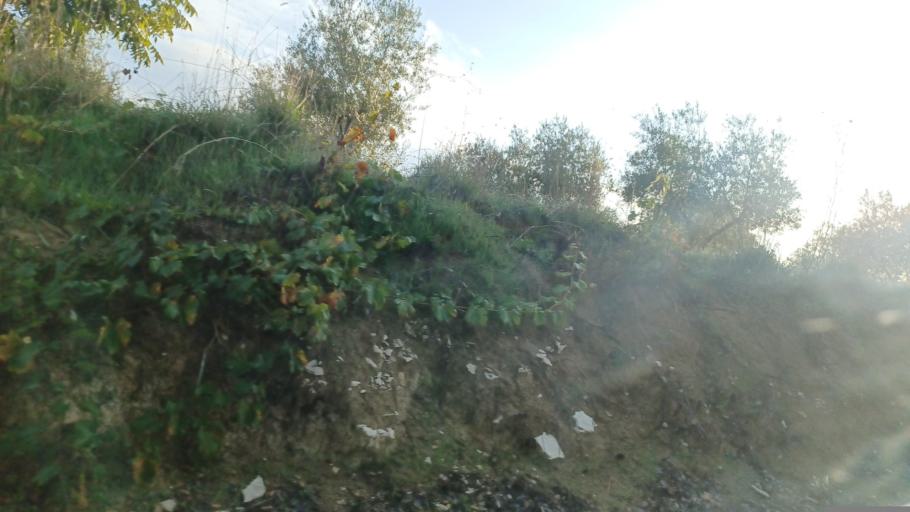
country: CY
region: Pafos
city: Tala
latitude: 34.8925
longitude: 32.4779
